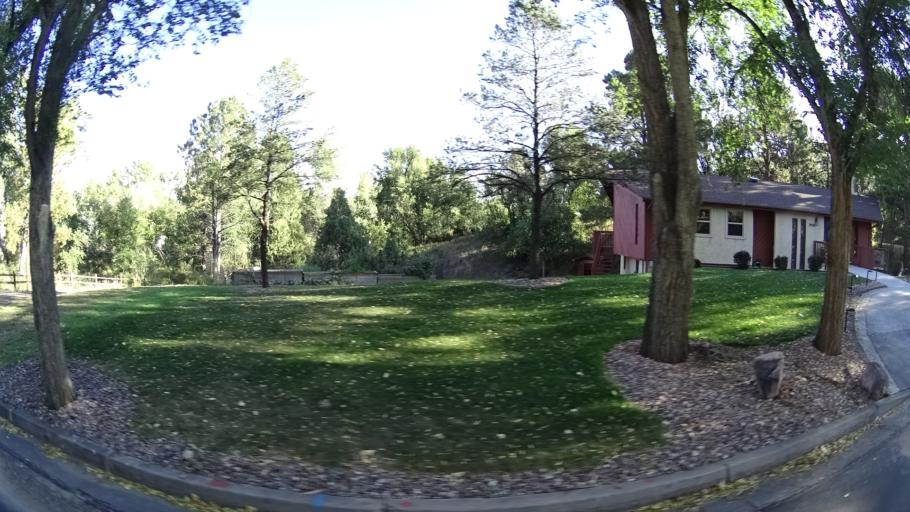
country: US
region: Colorado
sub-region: El Paso County
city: Colorado Springs
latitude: 38.8880
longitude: -104.7718
